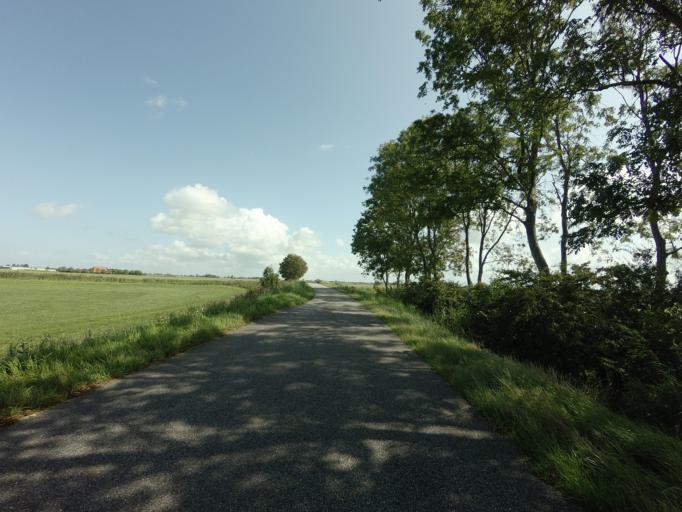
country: NL
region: Friesland
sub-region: Sudwest Fryslan
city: Makkum
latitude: 53.0646
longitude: 5.4493
